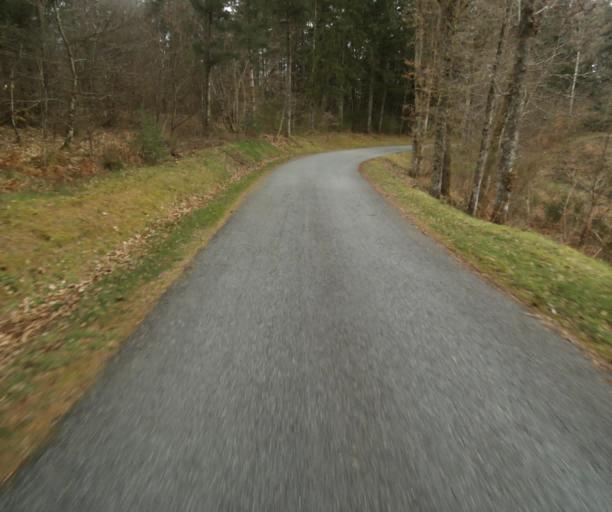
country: FR
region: Limousin
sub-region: Departement de la Correze
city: Correze
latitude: 45.2923
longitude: 1.9635
